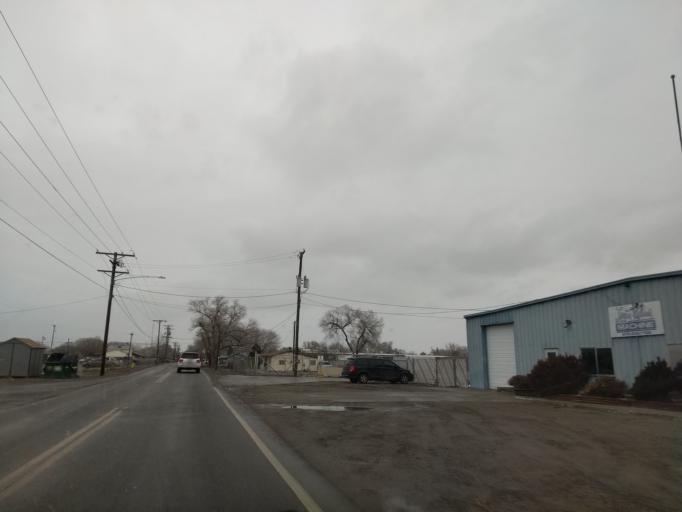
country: US
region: Colorado
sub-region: Mesa County
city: Grand Junction
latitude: 39.0720
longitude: -108.5244
